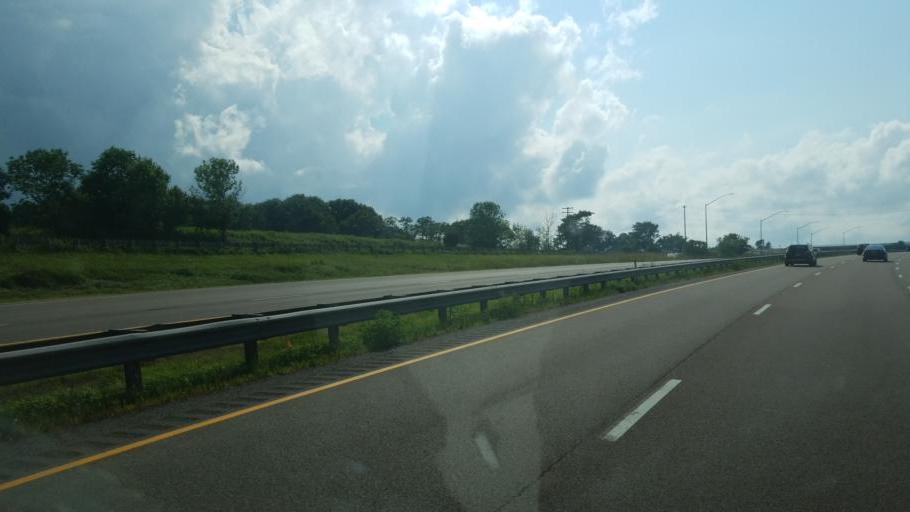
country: US
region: Pennsylvania
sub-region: Somerset County
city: Meyersdale
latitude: 39.6926
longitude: -79.1529
